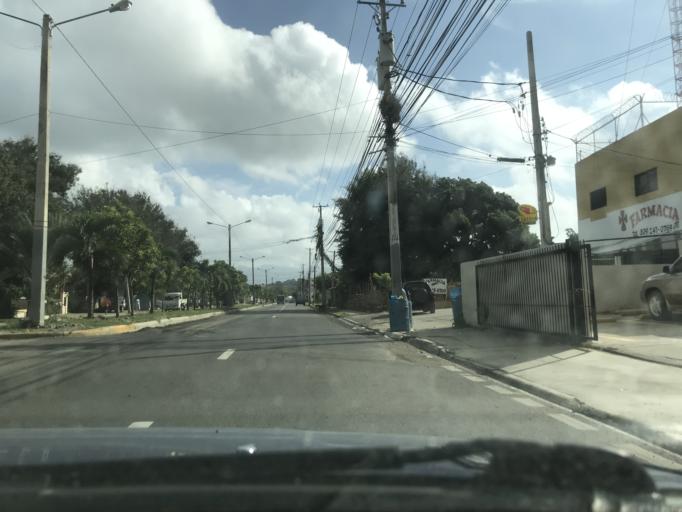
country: DO
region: Santiago
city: Santiago de los Caballeros
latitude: 19.4327
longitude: -70.7250
